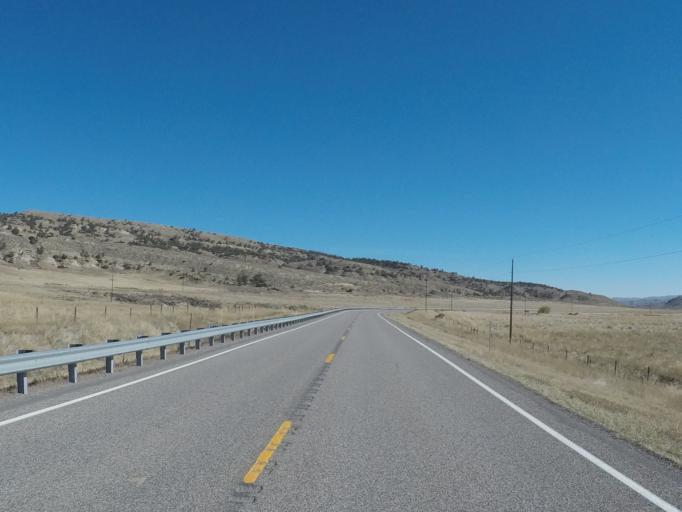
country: US
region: Montana
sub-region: Carbon County
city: Red Lodge
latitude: 45.1656
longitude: -109.1029
